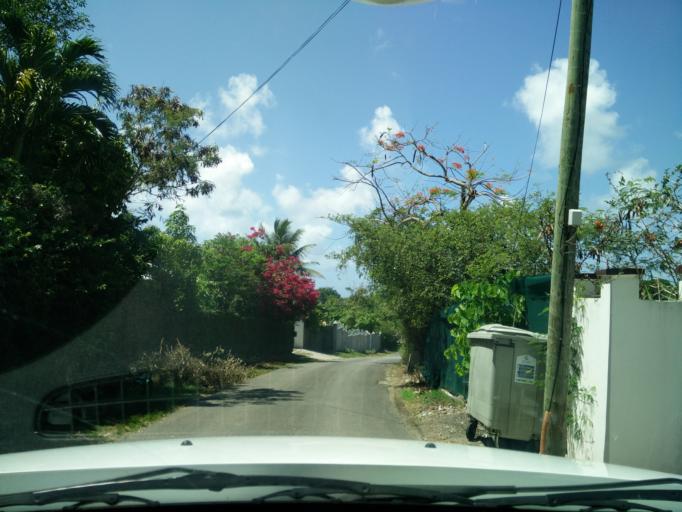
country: GP
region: Guadeloupe
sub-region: Guadeloupe
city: Sainte-Anne
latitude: 16.2449
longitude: -61.3424
